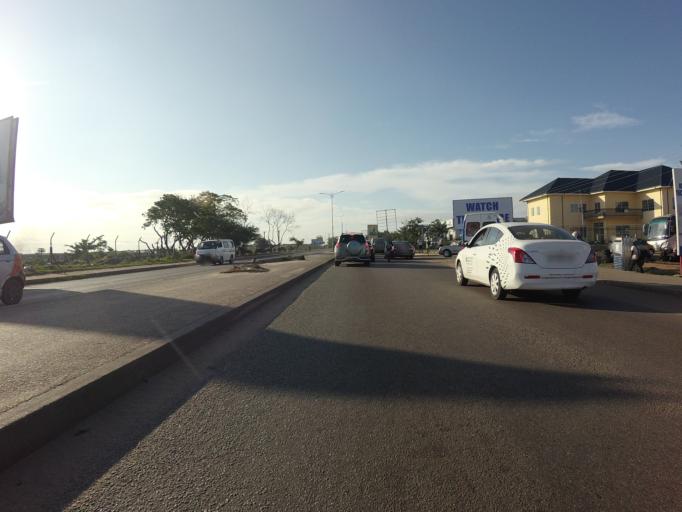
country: GH
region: Greater Accra
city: Accra
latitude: 5.5529
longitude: -0.2310
